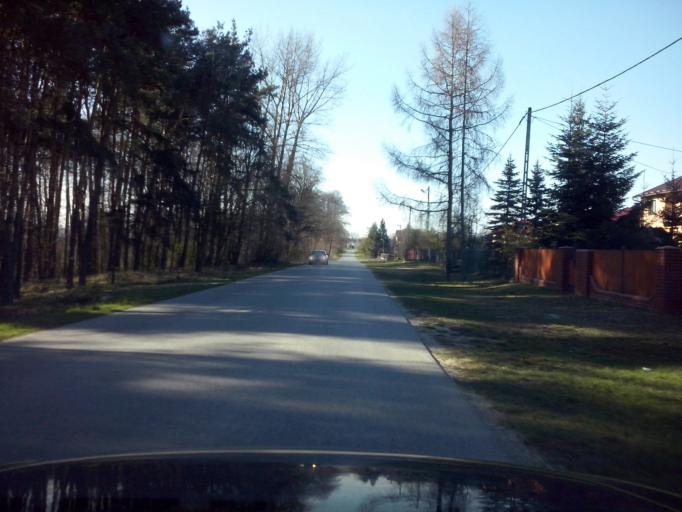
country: PL
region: Subcarpathian Voivodeship
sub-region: Powiat lezajski
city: Stare Miasto
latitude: 50.3643
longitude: 22.4173
